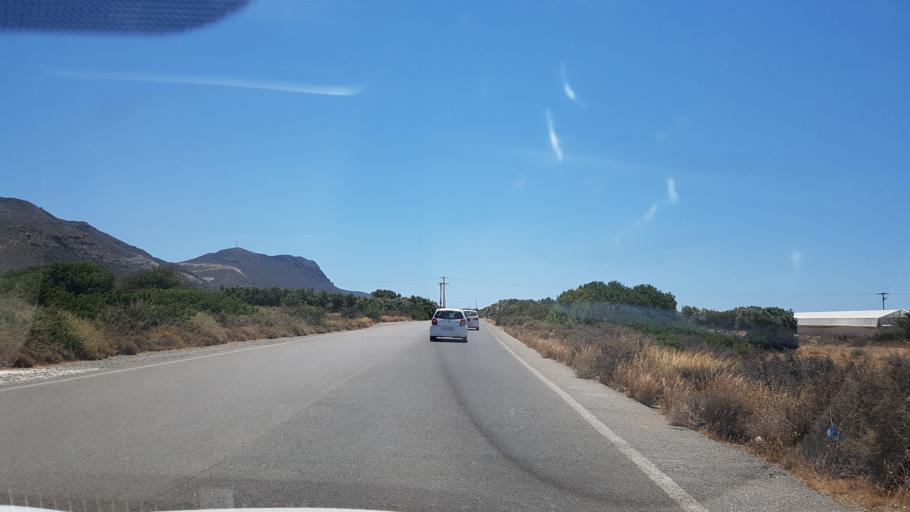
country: GR
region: Crete
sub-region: Nomos Chanias
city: Palaiochora
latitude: 35.2919
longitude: 23.5454
